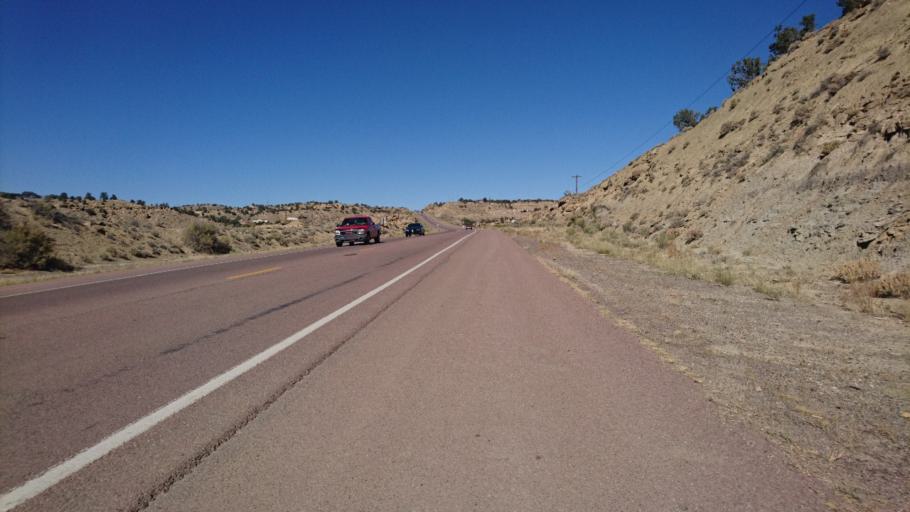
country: US
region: New Mexico
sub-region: McKinley County
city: Gallup
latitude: 35.4668
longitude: -108.7428
